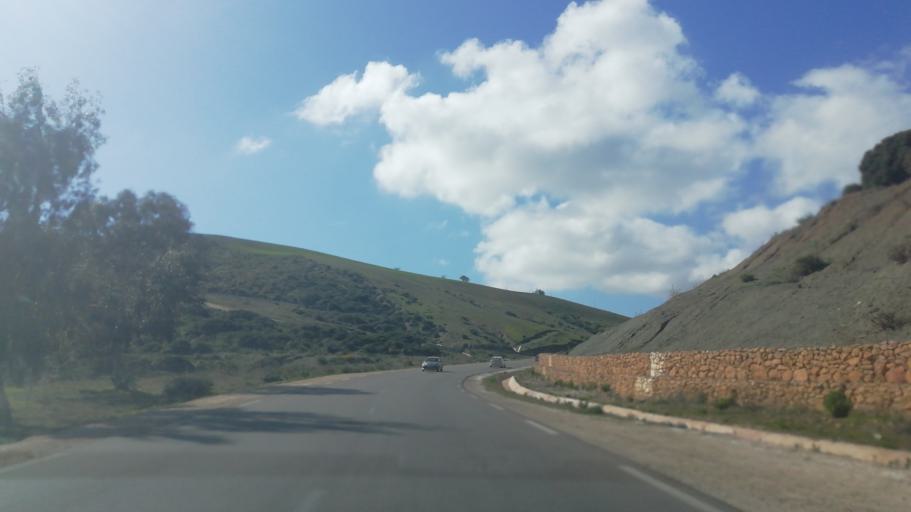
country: DZ
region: Relizane
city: Relizane
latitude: 36.0819
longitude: 0.4811
